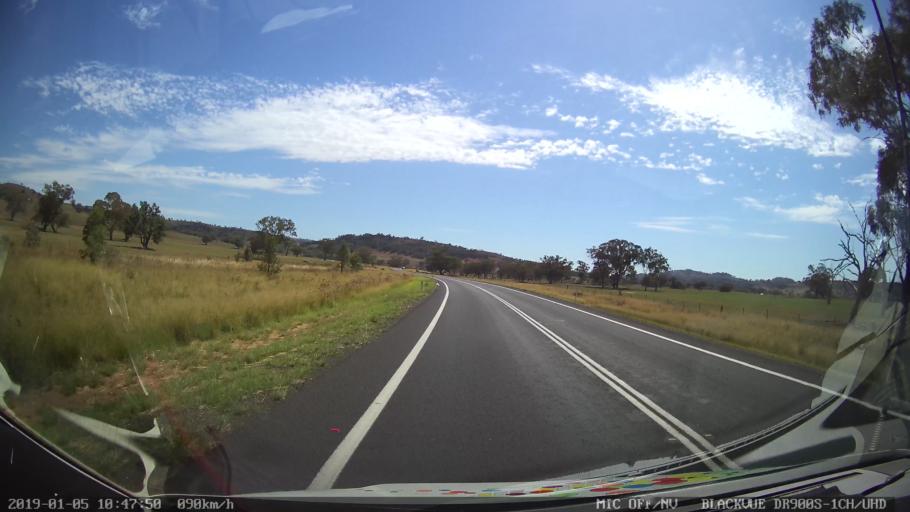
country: AU
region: New South Wales
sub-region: Warrumbungle Shire
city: Coonabarabran
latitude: -31.4416
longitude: 149.0381
